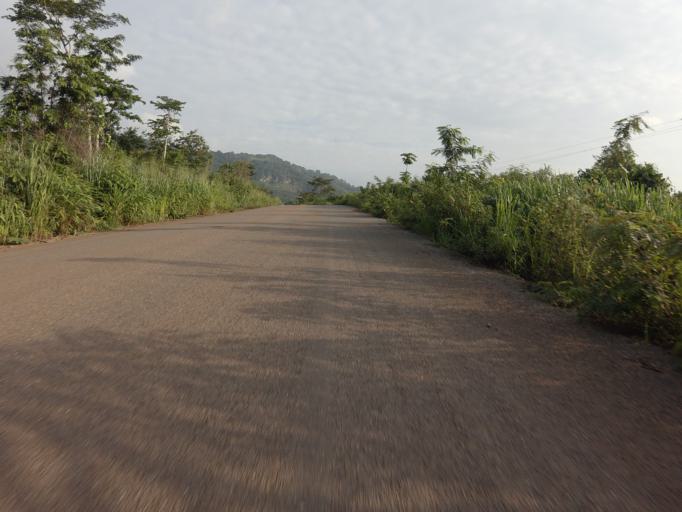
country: TG
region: Plateaux
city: Kpalime
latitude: 6.9288
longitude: 0.4620
